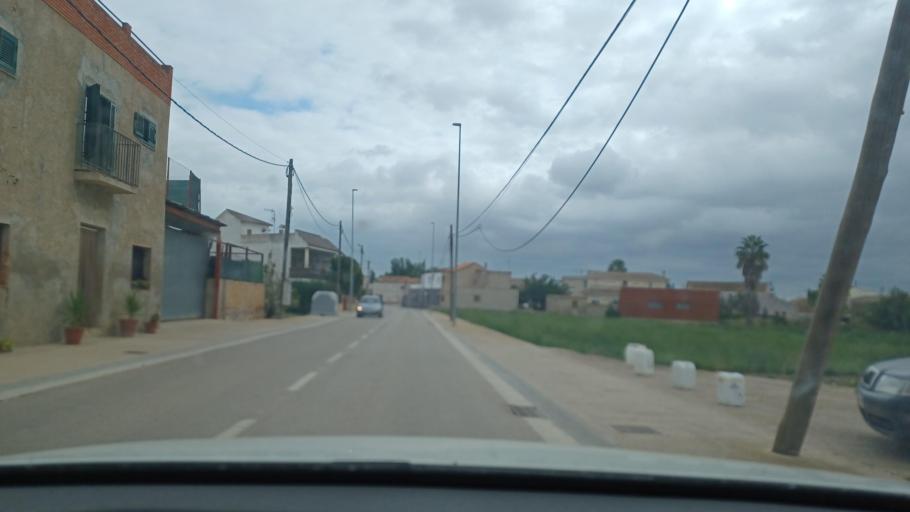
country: ES
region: Catalonia
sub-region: Provincia de Tarragona
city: Deltebre
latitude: 40.7257
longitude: 0.6924
